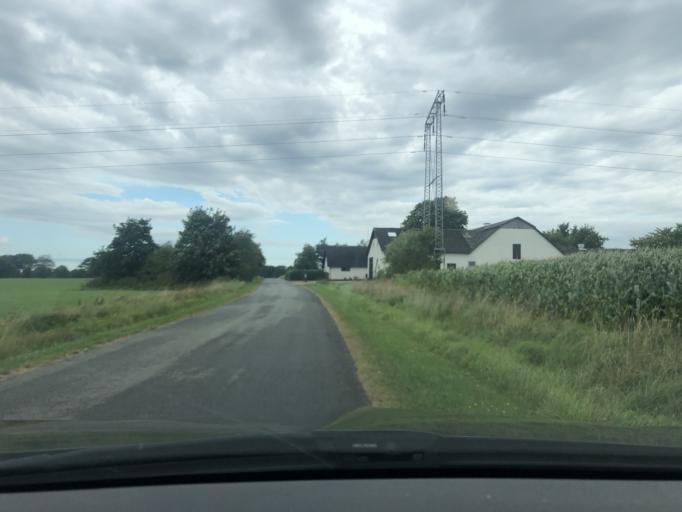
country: DK
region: South Denmark
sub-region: Varde Kommune
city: Olgod
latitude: 55.8083
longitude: 8.6878
